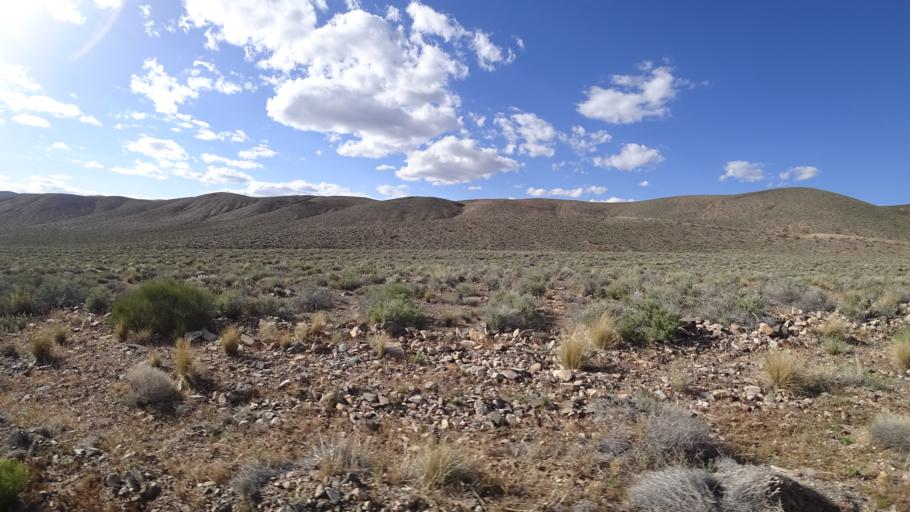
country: US
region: California
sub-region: San Bernardino County
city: Searles Valley
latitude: 36.3063
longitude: -117.1519
